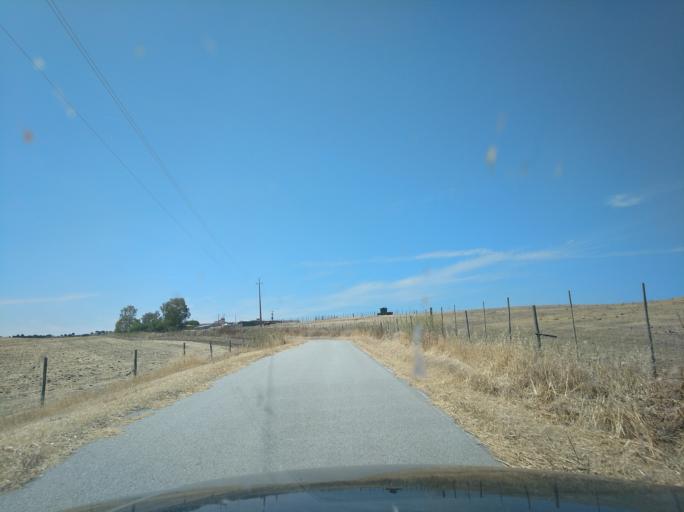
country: PT
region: Portalegre
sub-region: Campo Maior
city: Campo Maior
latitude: 38.9623
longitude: -7.1120
